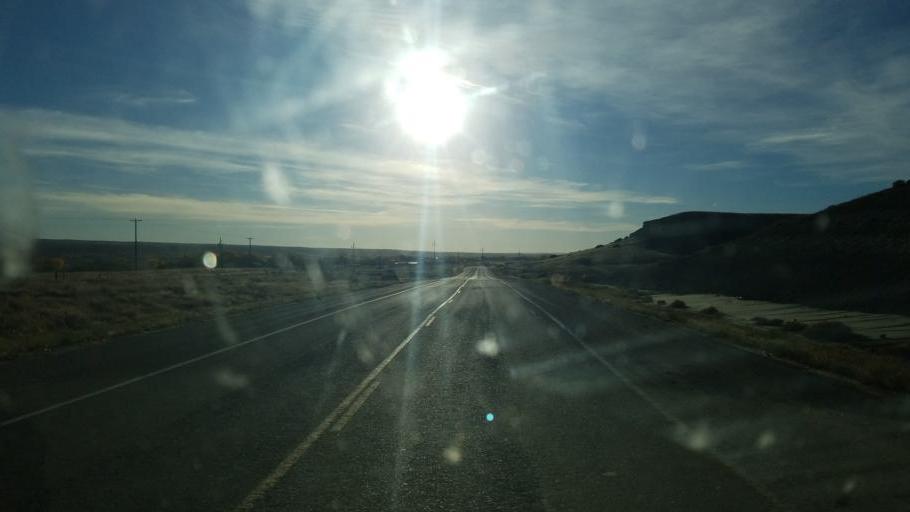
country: US
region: New Mexico
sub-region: San Juan County
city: Bloomfield
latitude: 36.7127
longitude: -107.8446
